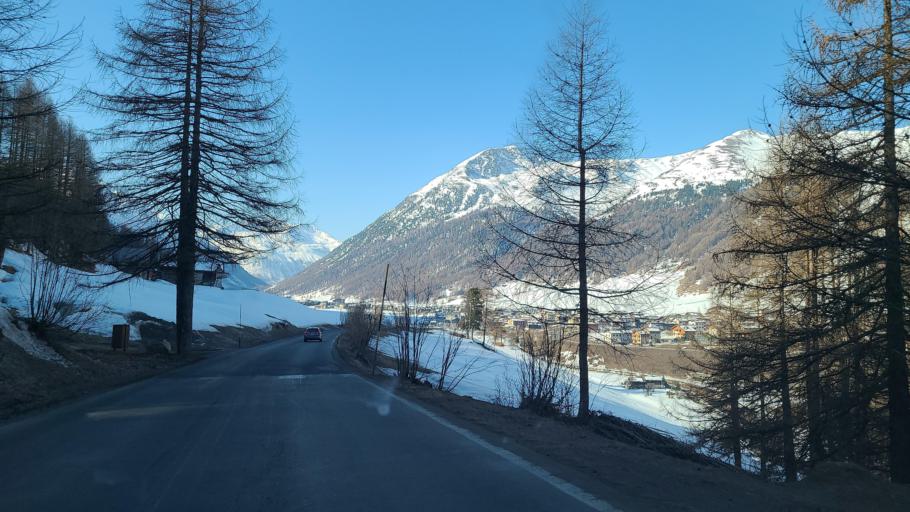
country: IT
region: Lombardy
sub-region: Provincia di Sondrio
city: Livigno
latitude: 46.5247
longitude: 10.1327
